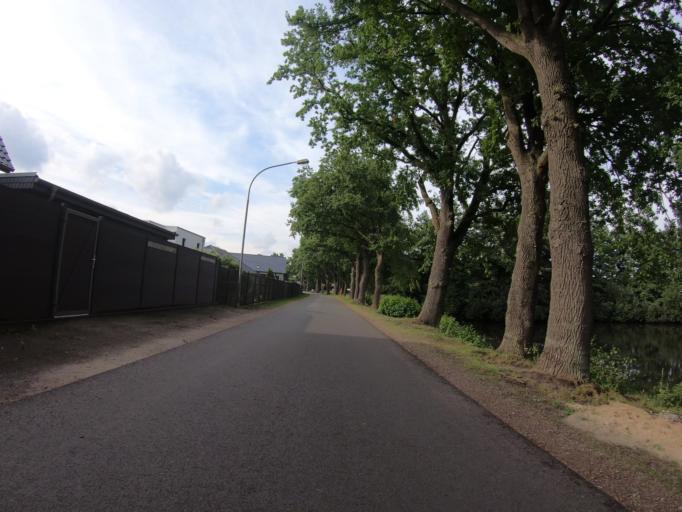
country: DE
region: Lower Saxony
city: Gifhorn
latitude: 52.5033
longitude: 10.5870
